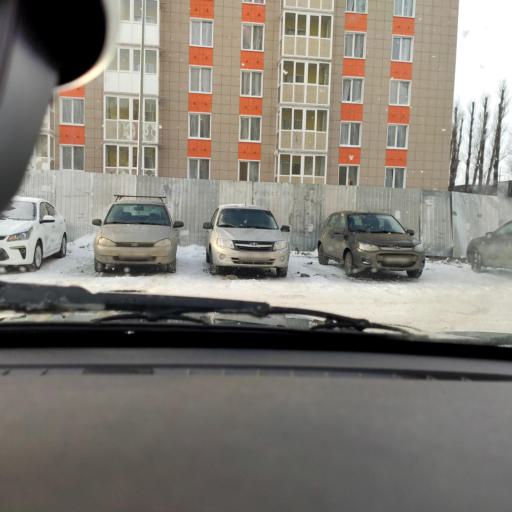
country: RU
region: Samara
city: Tol'yatti
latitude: 53.5487
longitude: 49.3125
